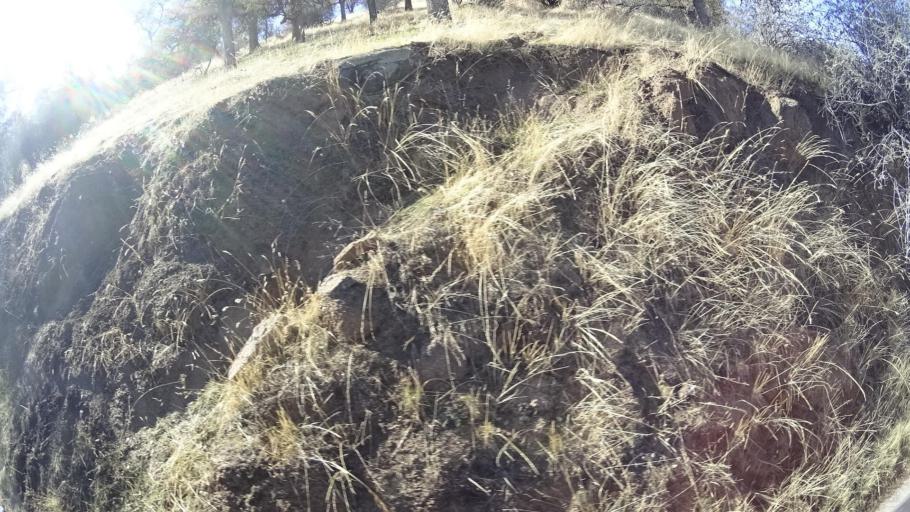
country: US
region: California
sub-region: Kern County
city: Bodfish
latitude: 35.4422
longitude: -118.6891
